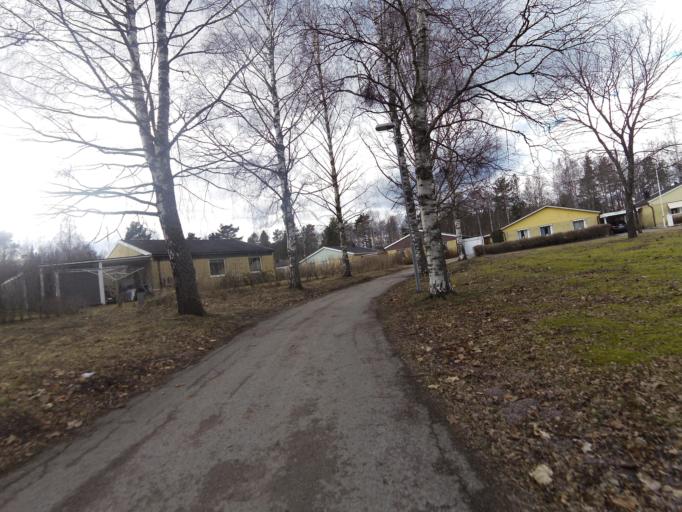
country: SE
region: Gaevleborg
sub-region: Gavle Kommun
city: Gavle
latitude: 60.6975
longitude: 17.1104
